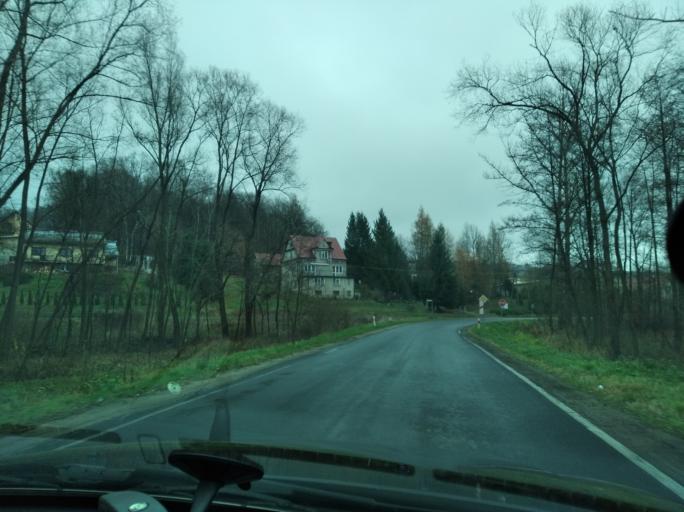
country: PL
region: Subcarpathian Voivodeship
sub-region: Powiat przeworski
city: Jawornik Polski
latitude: 49.8896
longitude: 22.2677
